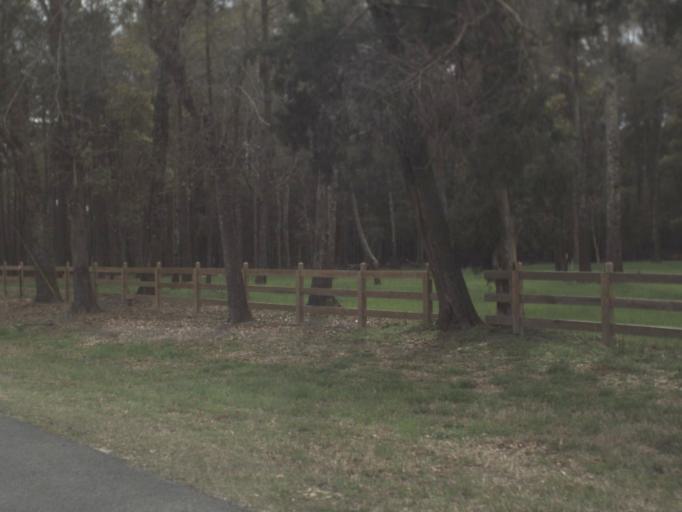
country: US
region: Florida
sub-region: Gadsden County
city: Quincy
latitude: 30.5137
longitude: -84.6092
